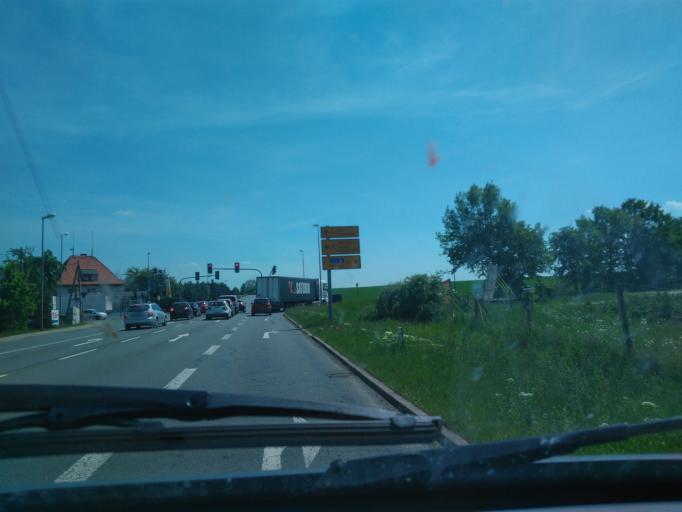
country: DE
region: Thuringia
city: Umpferstedt
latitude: 50.9749
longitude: 11.4108
